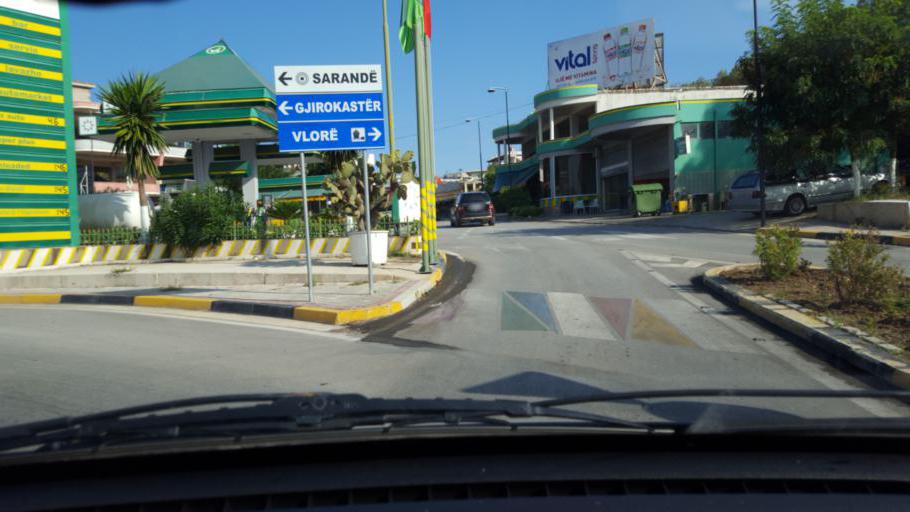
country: AL
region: Vlore
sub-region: Rrethi i Sarandes
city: Sarande
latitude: 39.8752
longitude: 20.0273
